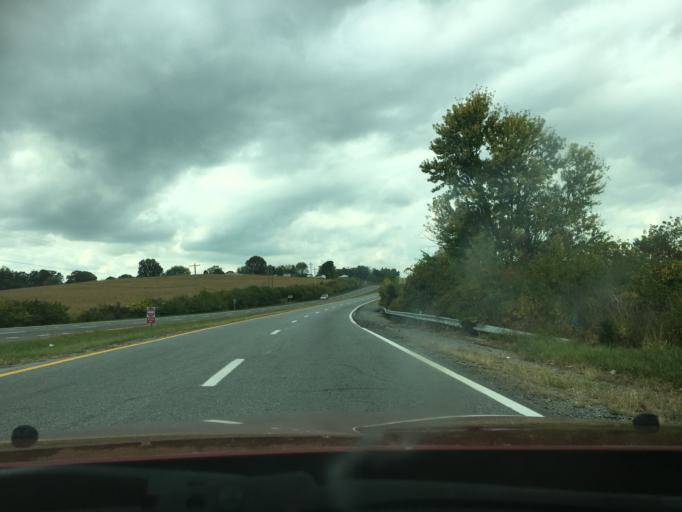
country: US
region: Virginia
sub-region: Pulaski County
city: Fairlawn
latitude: 37.1560
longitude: -80.5620
